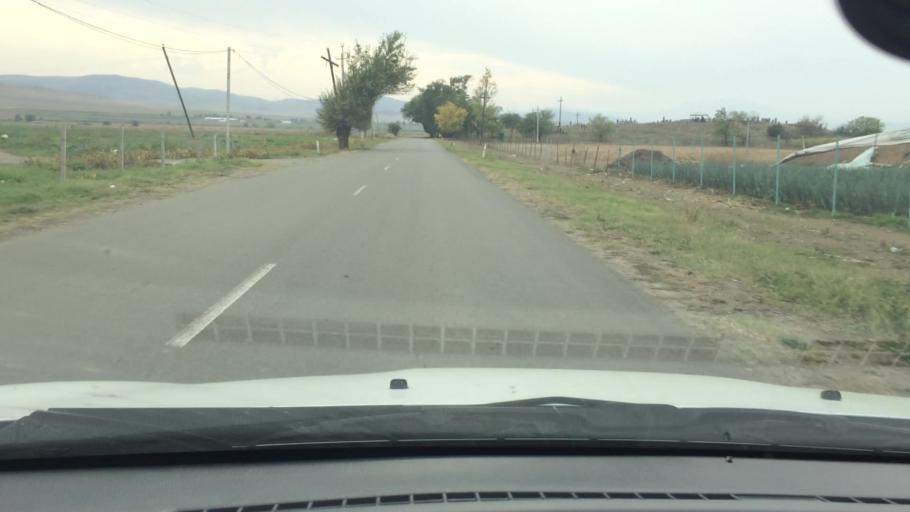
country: AM
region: Tavush
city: Berdavan
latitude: 41.3515
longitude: 44.9616
